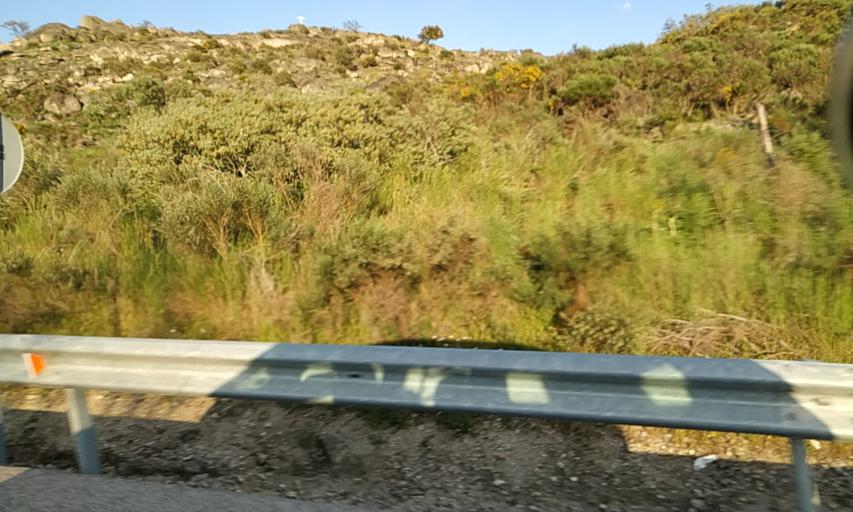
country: ES
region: Extremadura
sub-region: Provincia de Caceres
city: Valencia de Alcantara
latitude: 39.3798
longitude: -7.2511
